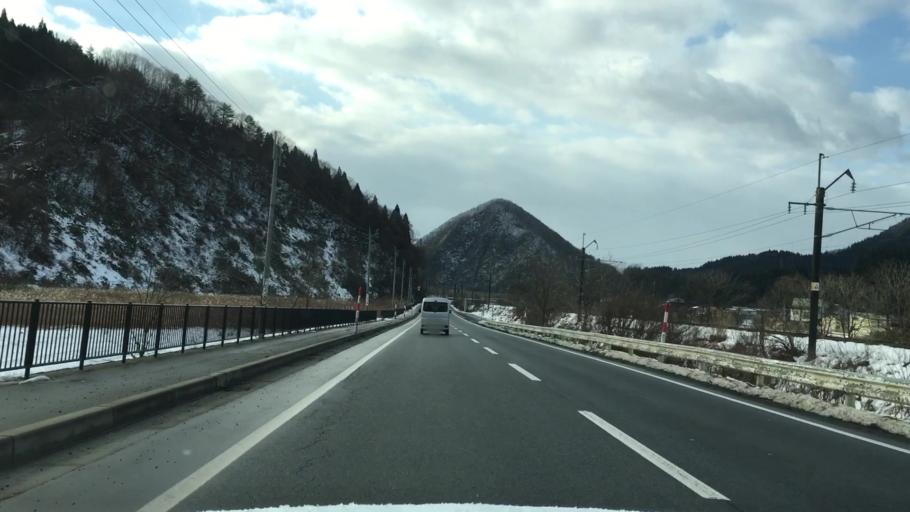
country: JP
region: Akita
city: Odate
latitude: 40.3697
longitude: 140.5994
